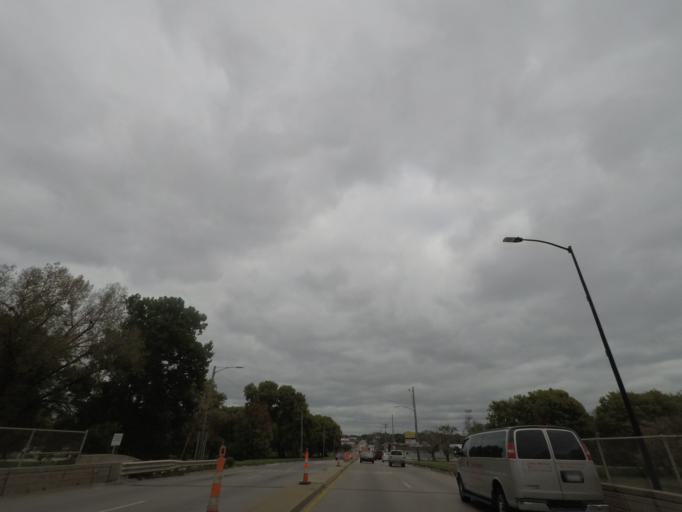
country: US
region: Iowa
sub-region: Polk County
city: Des Moines
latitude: 41.5767
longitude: -93.5969
